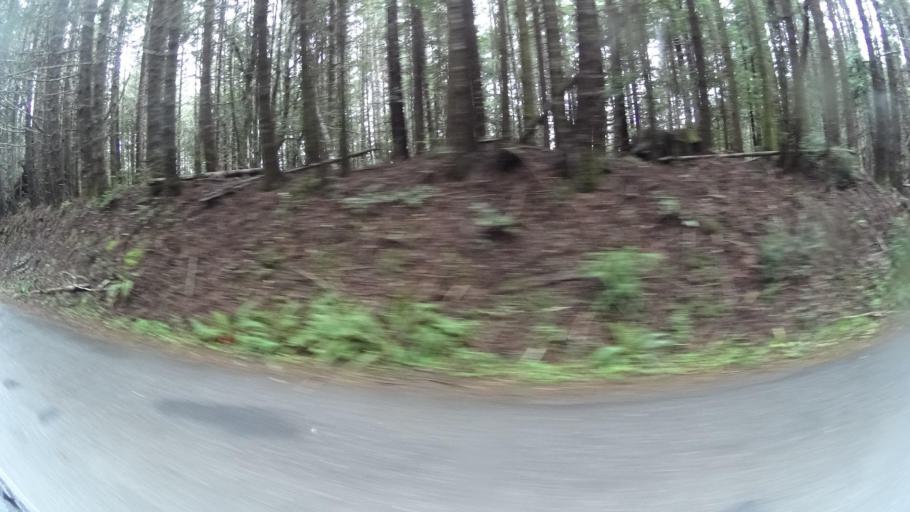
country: US
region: California
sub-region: Humboldt County
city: Westhaven-Moonstone
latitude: 41.2443
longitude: -123.9821
